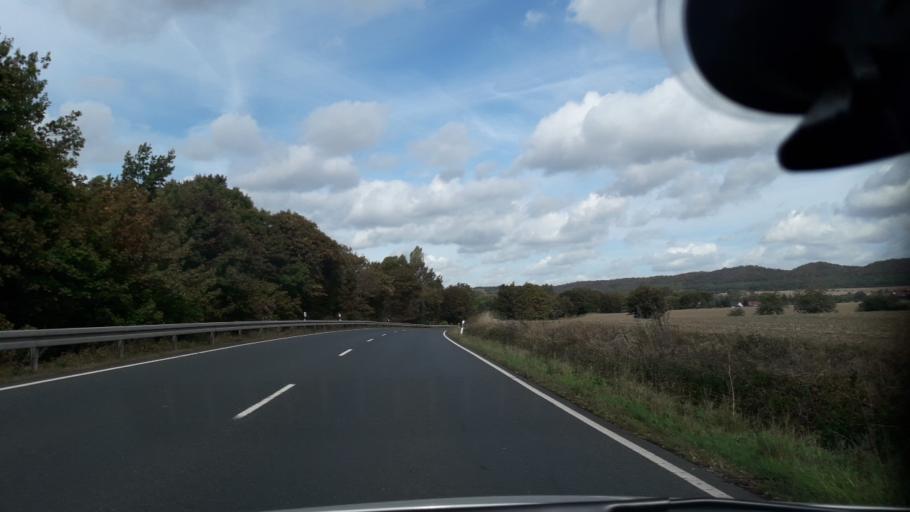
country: DE
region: Lower Saxony
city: Liebenburg
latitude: 51.9950
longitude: 10.3763
